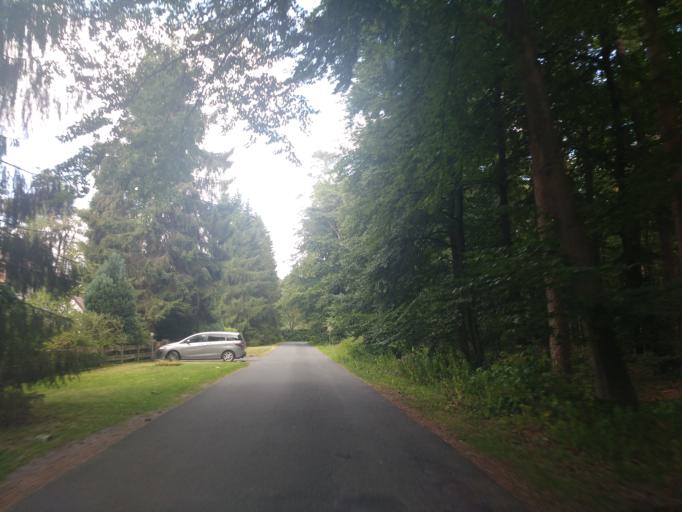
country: DE
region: North Rhine-Westphalia
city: Bad Lippspringe
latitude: 51.7985
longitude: 8.8175
